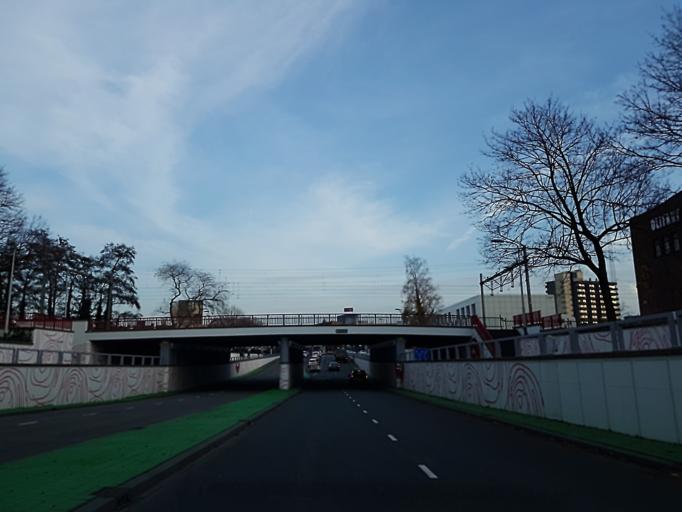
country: NL
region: North Brabant
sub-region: Roosendaal
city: Roosendaal
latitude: 51.5321
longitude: 4.4503
